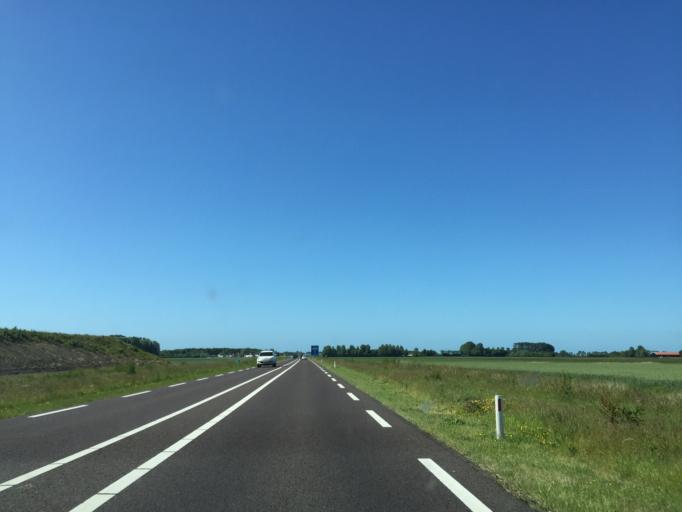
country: NL
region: Zeeland
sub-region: Gemeente Middelburg
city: Middelburg
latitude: 51.5333
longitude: 3.6106
